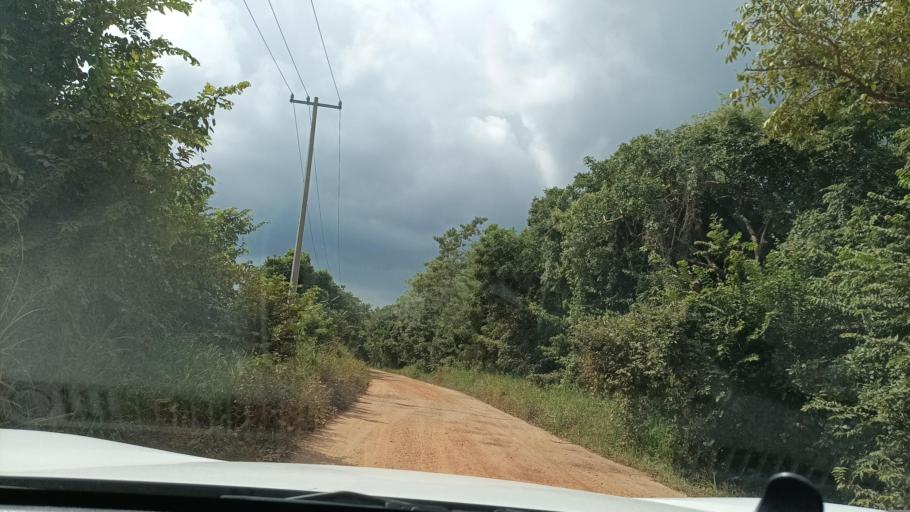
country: MX
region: Veracruz
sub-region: Chinameca
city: Chacalapa
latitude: 18.0826
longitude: -94.6853
